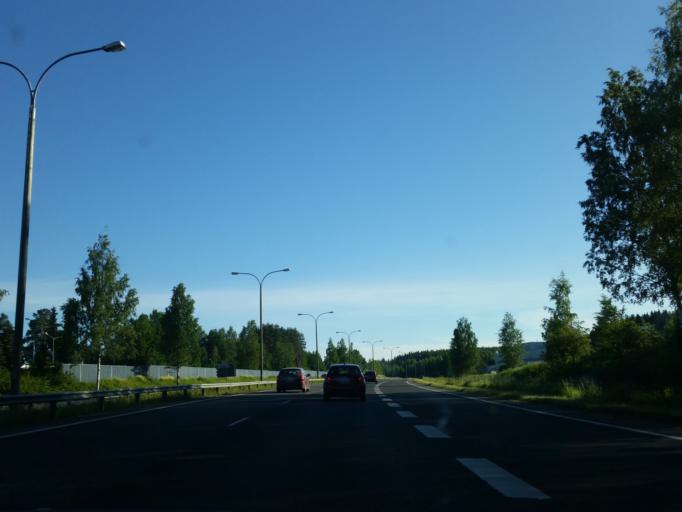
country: FI
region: Northern Savo
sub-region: Kuopio
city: Kuopio
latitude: 62.8807
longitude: 27.6318
